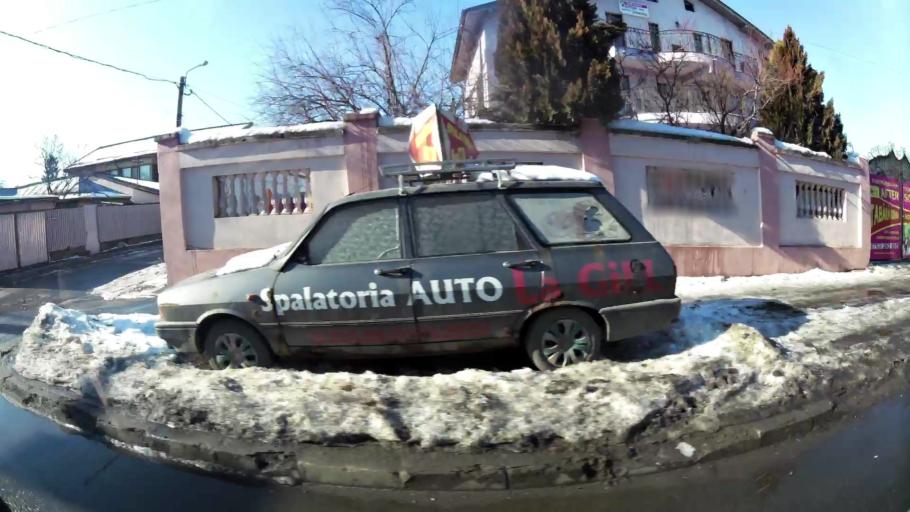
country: RO
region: Ilfov
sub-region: Comuna Magurele
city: Magurele
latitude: 44.3933
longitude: 26.0480
